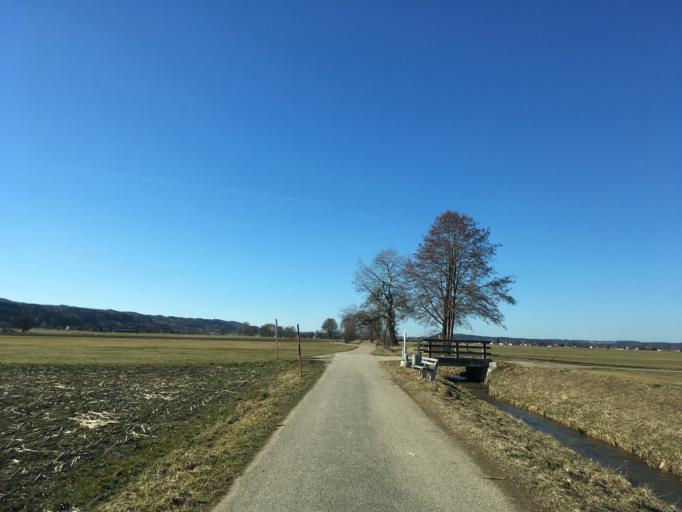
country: DE
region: Bavaria
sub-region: Upper Bavaria
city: Bad Aibling
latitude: 47.8547
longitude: 11.9673
